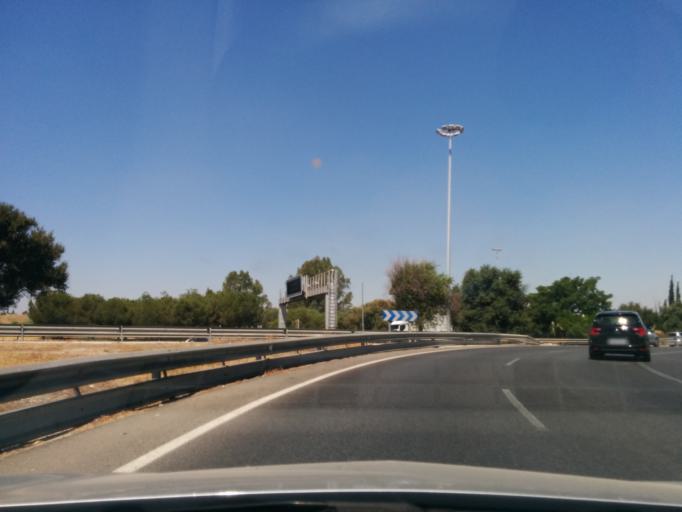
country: ES
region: Andalusia
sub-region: Provincia de Sevilla
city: San Juan de Aznalfarache
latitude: 37.3702
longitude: -6.0132
